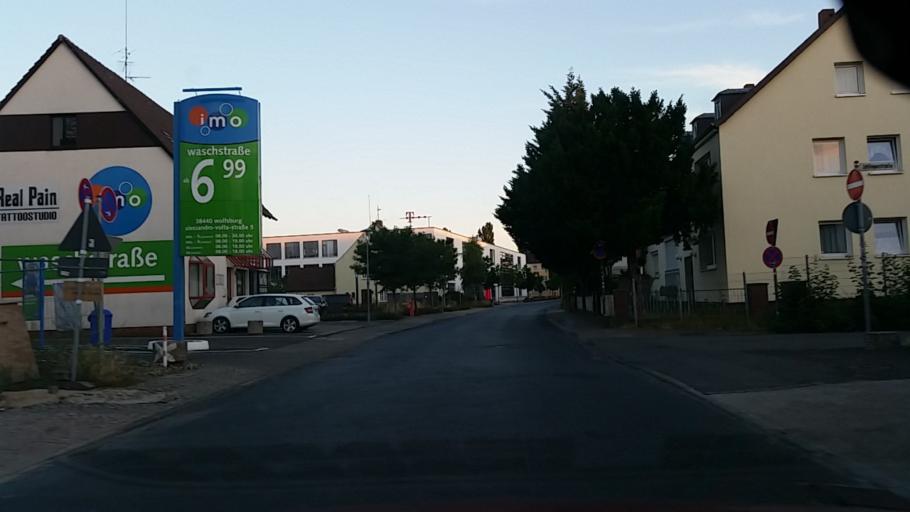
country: DE
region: Lower Saxony
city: Wolfsburg
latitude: 52.4267
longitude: 10.7919
